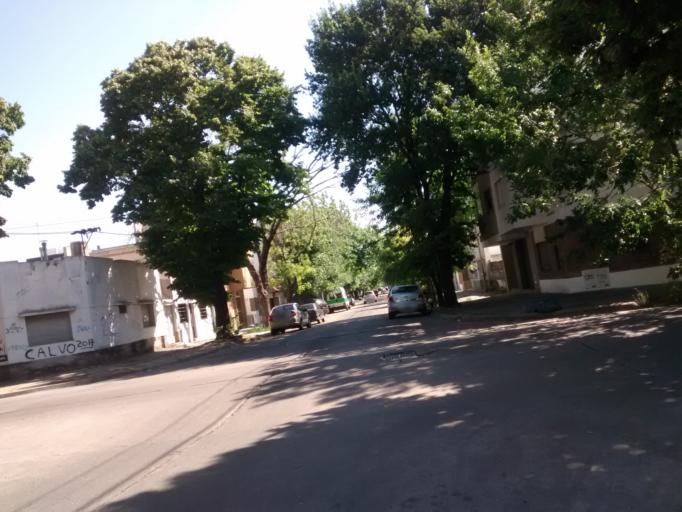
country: AR
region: Buenos Aires
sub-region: Partido de La Plata
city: La Plata
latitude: -34.9067
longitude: -57.9695
